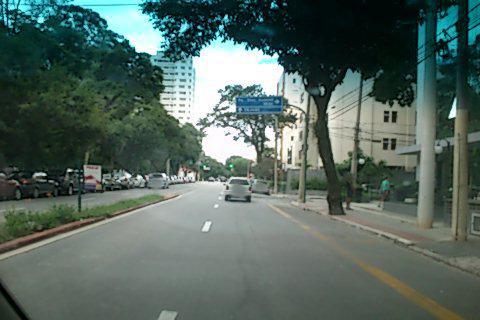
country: BR
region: Sao Paulo
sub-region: Sao Jose Dos Campos
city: Sao Jose dos Campos
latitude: -23.1990
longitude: -45.8952
